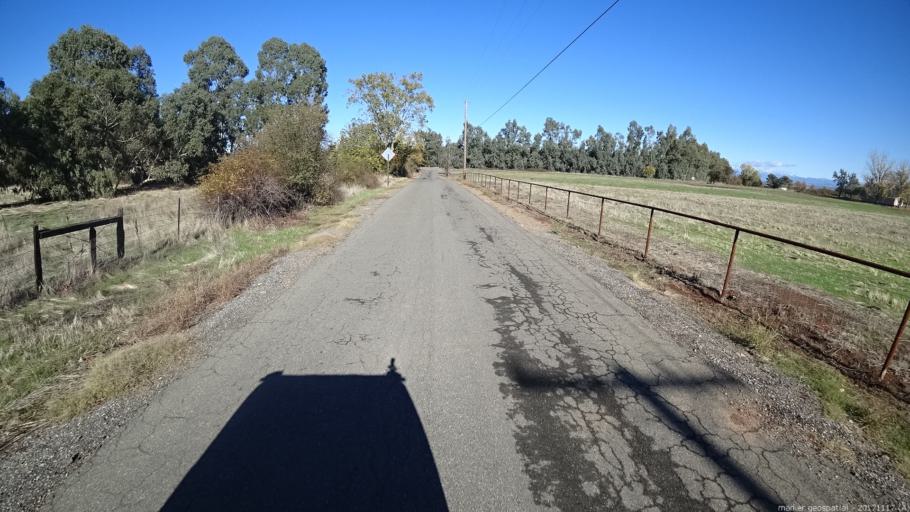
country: US
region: California
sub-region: Shasta County
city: Anderson
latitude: 40.4306
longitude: -122.2593
